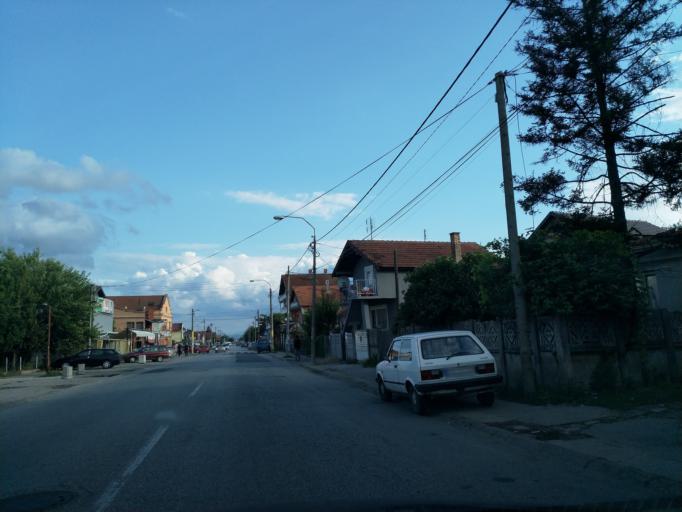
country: RS
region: Central Serbia
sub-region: Pomoravski Okrug
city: Paracin
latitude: 43.8516
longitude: 21.4132
